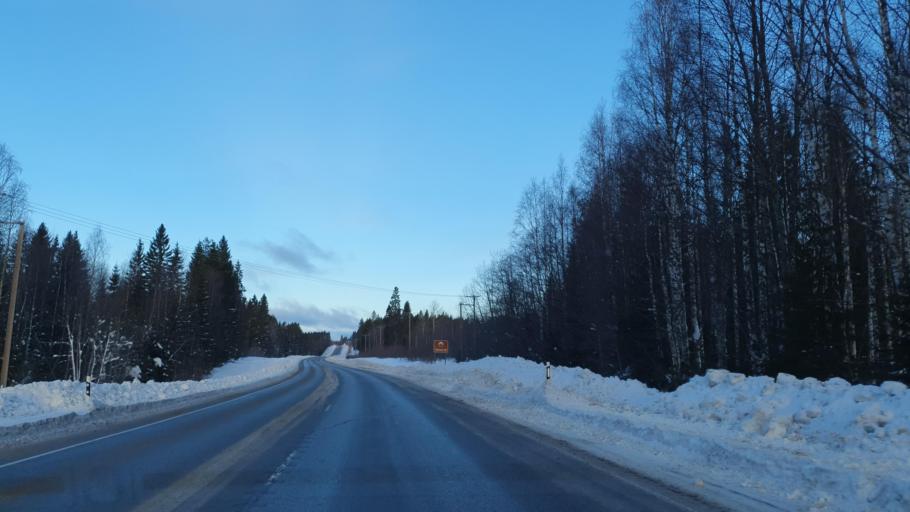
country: FI
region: Kainuu
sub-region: Kajaani
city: Paltamo
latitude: 64.3825
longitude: 28.0159
